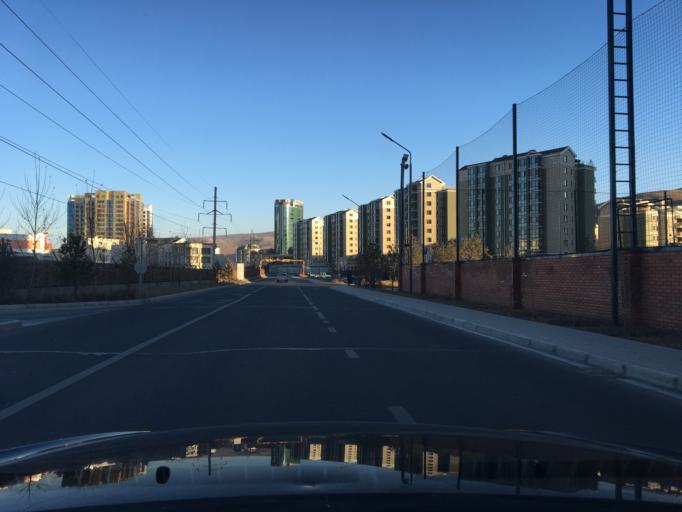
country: MN
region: Ulaanbaatar
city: Ulaanbaatar
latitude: 47.8917
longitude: 106.9276
